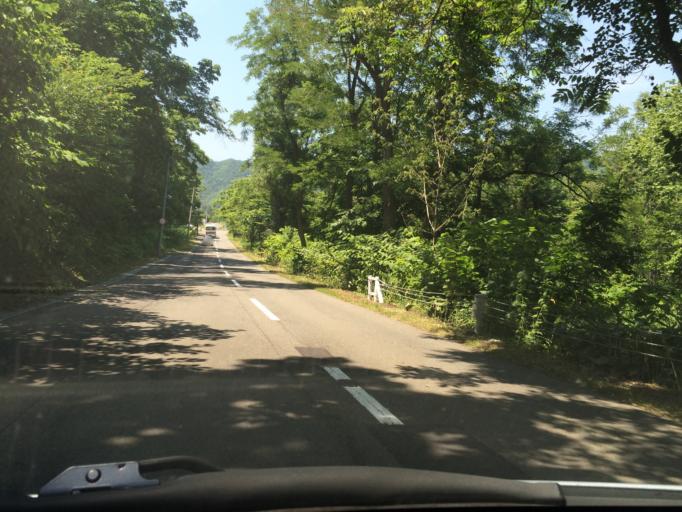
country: JP
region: Hokkaido
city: Sapporo
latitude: 42.9645
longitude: 141.2767
